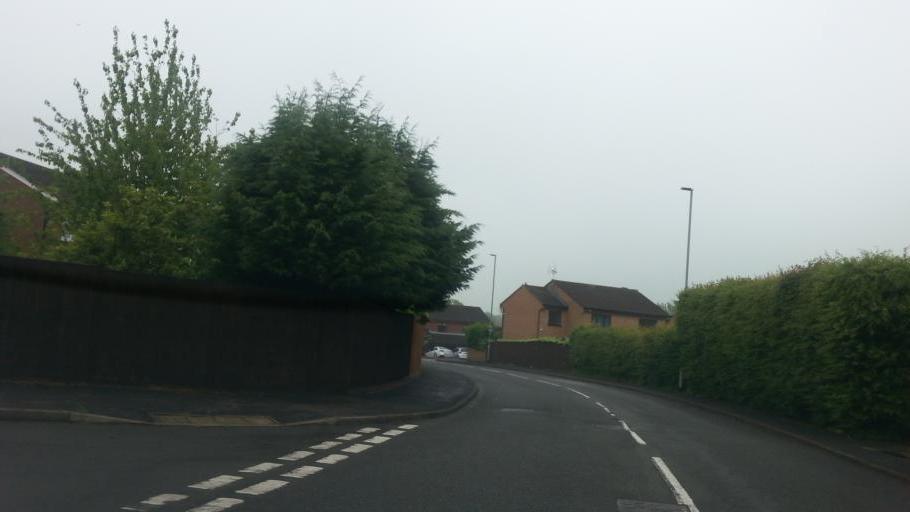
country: GB
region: England
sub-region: Leicestershire
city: Oadby
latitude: 52.5941
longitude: -1.0592
